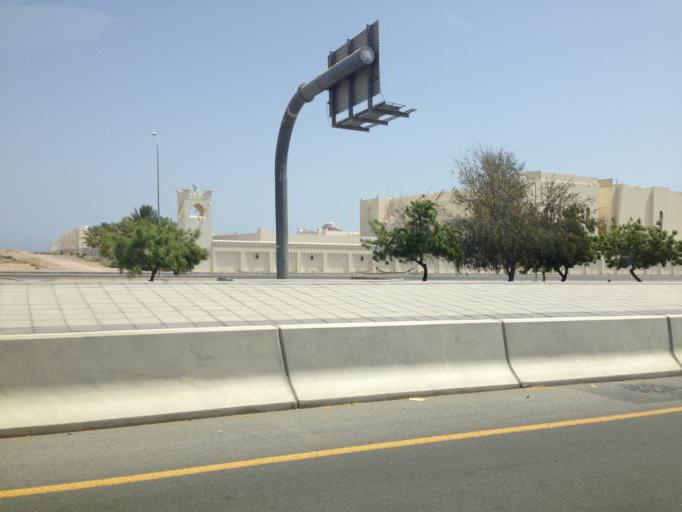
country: OM
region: Muhafazat Masqat
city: Bawshar
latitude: 23.6043
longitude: 58.3279
